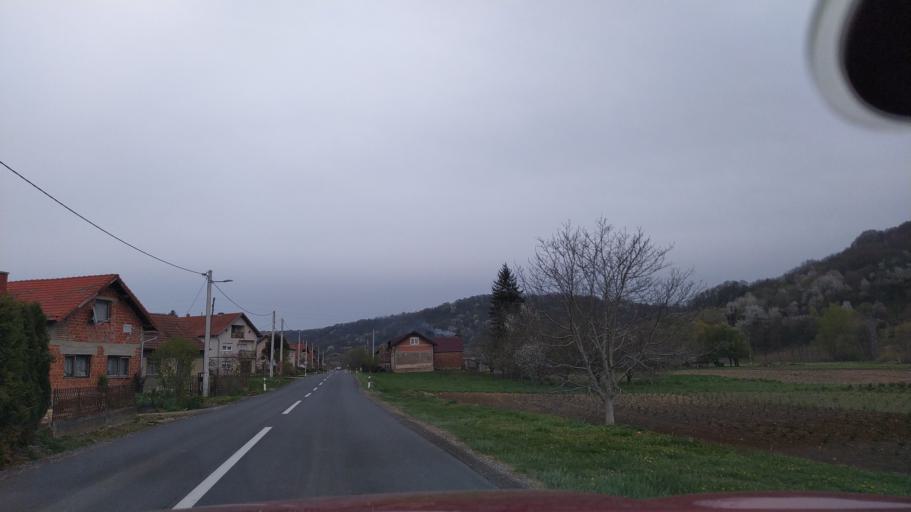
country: HR
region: Varazdinska
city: Jalzabet
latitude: 46.2113
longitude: 16.4723
